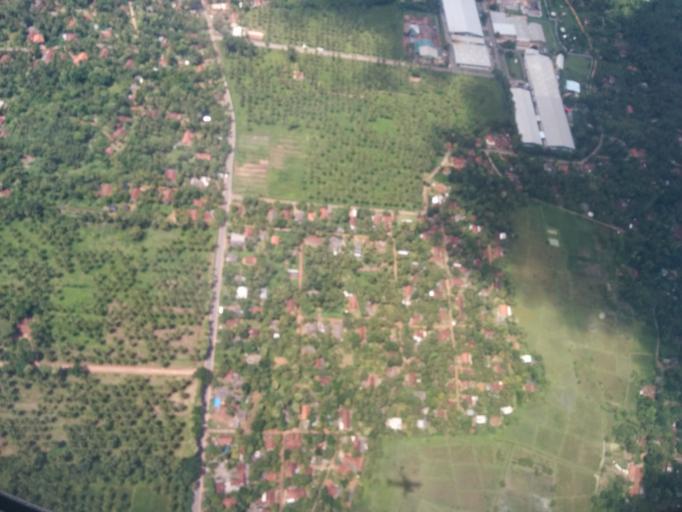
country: LK
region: Western
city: Minuwangoda
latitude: 7.3181
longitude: 79.9765
